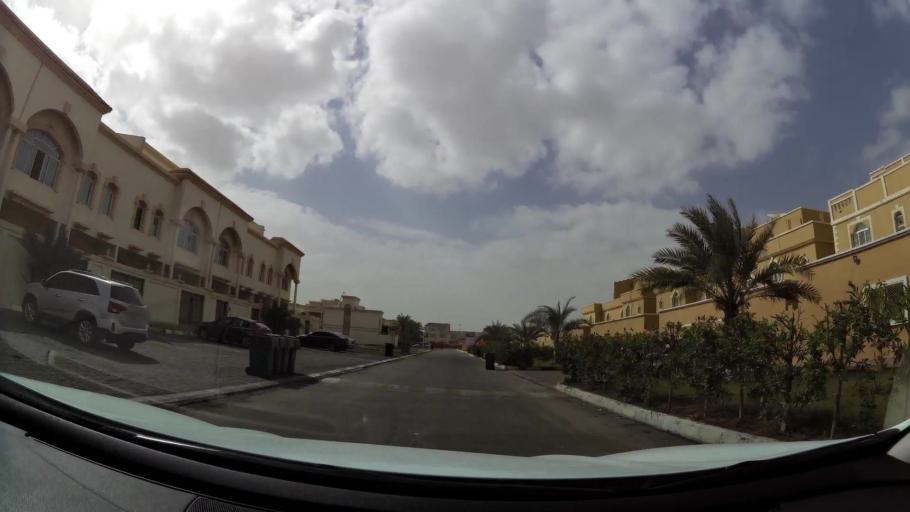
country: AE
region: Abu Dhabi
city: Abu Dhabi
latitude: 24.4076
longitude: 54.4940
